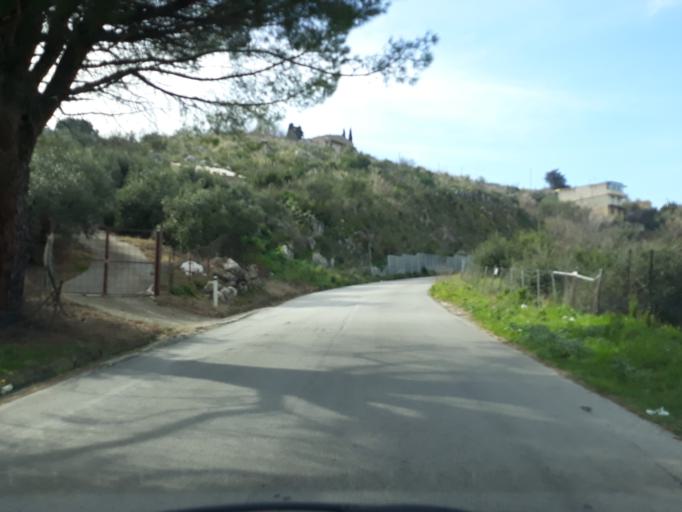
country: IT
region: Sicily
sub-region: Palermo
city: Altofonte
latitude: 38.0405
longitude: 13.3110
